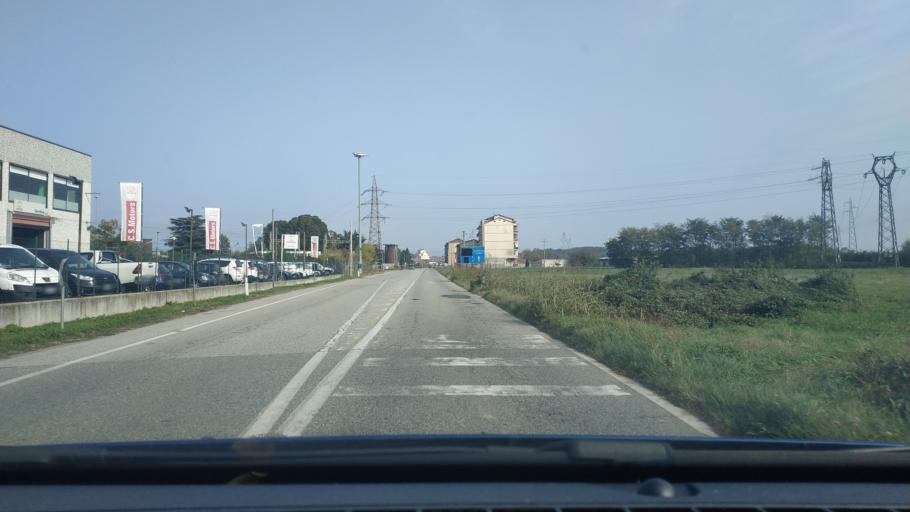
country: IT
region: Piedmont
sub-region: Provincia di Torino
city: Scarmagno
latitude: 45.3769
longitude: 7.8551
